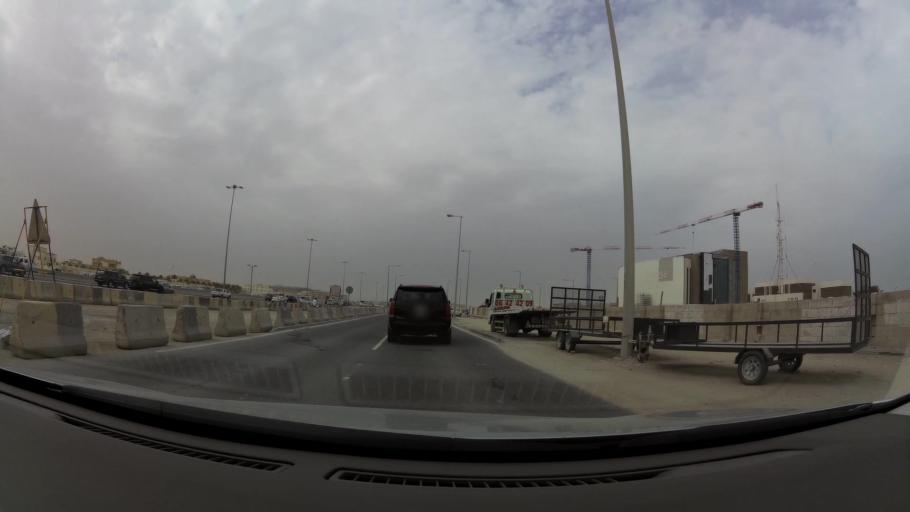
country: QA
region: Baladiyat ar Rayyan
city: Ar Rayyan
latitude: 25.3507
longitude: 51.4553
